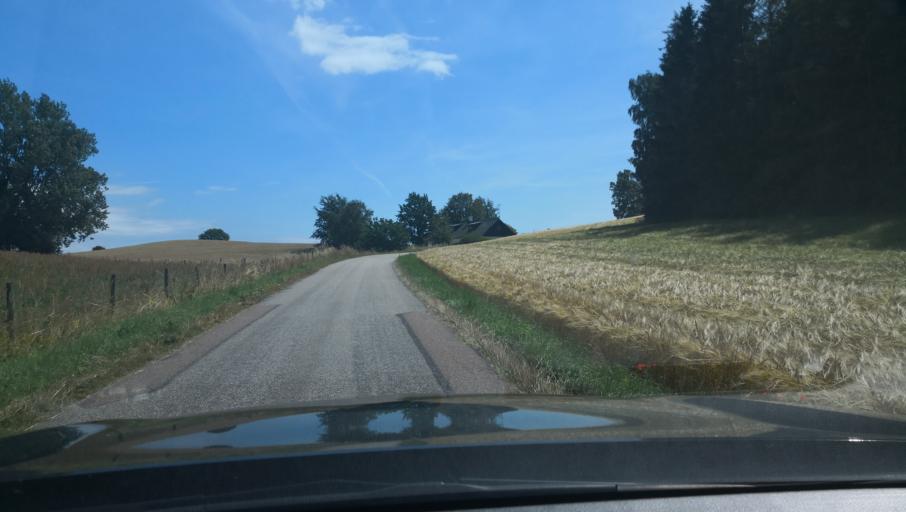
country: SE
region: Skane
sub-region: Ystads Kommun
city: Kopingebro
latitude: 55.3907
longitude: 14.1405
